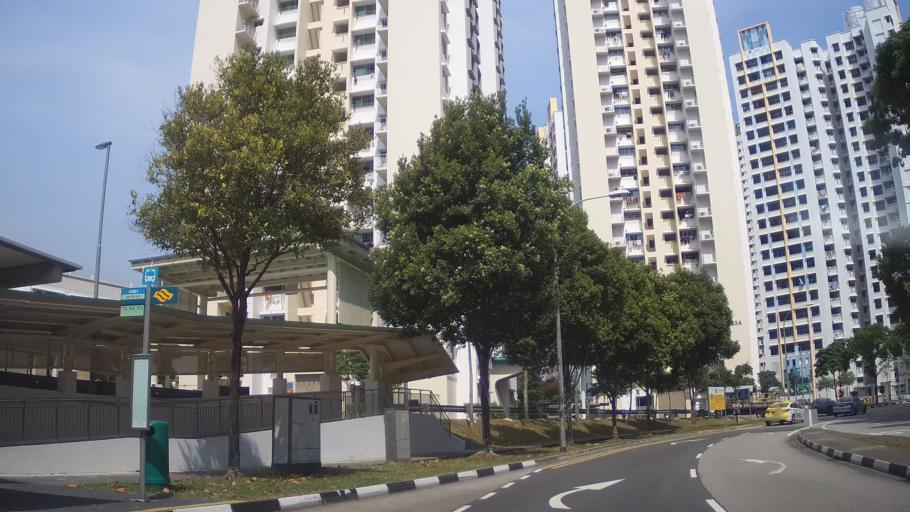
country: MY
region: Johor
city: Johor Bahru
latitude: 1.3852
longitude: 103.7593
